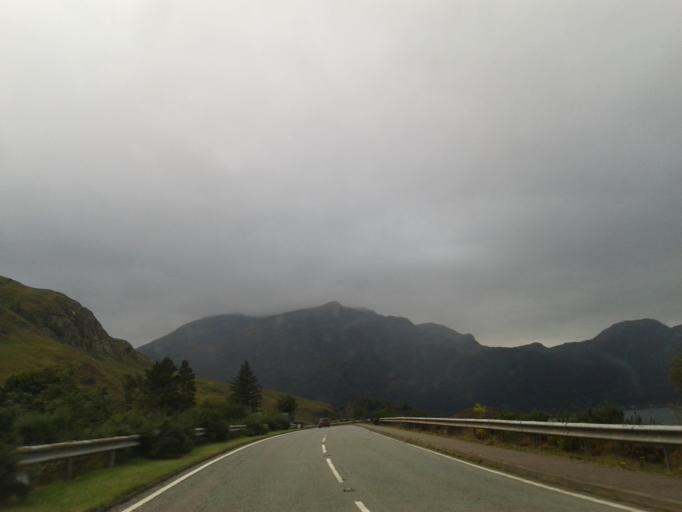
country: GB
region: Scotland
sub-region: Highland
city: Fort William
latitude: 57.2291
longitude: -5.4035
